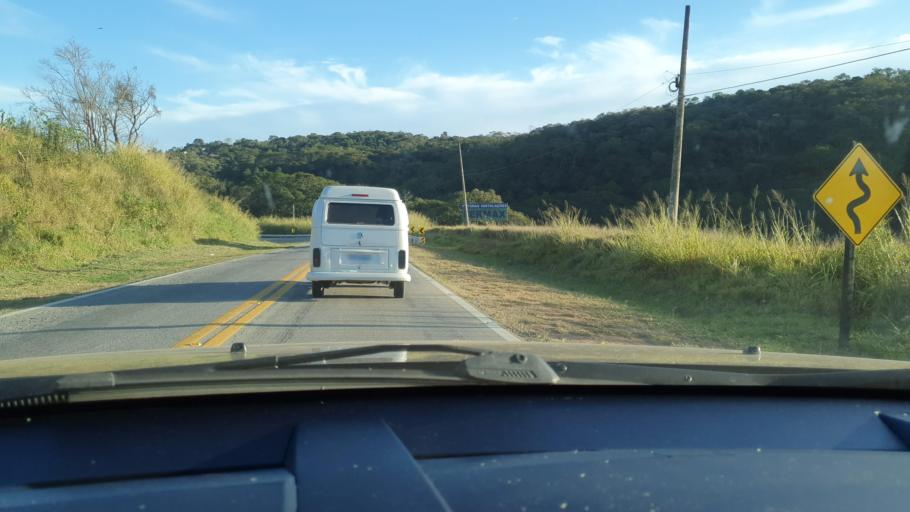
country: BR
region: Sao Paulo
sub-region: Piedade
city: Piedade
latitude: -23.7139
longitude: -47.3939
